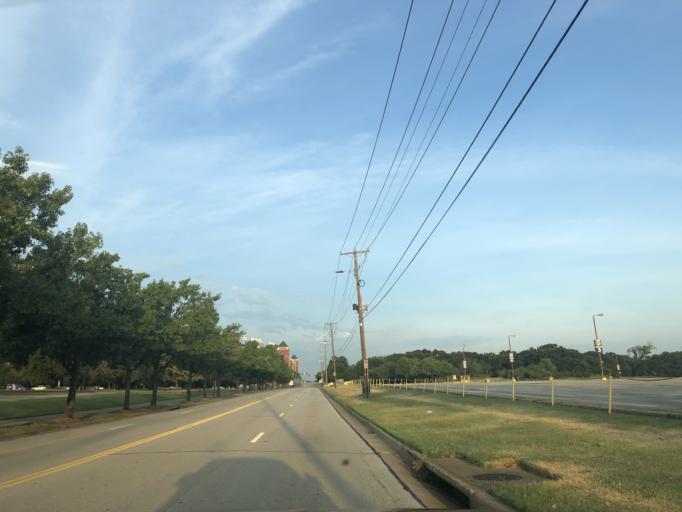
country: US
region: Texas
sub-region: Tarrant County
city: Arlington
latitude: 32.7525
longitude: -97.0764
